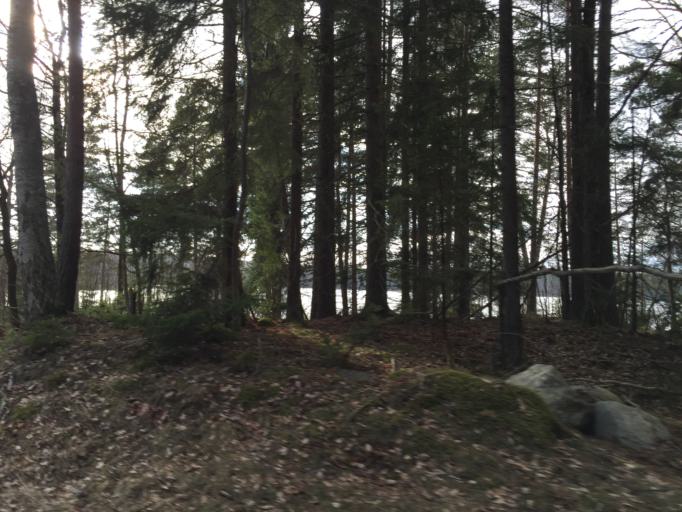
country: SE
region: Soedermanland
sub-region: Vingakers Kommun
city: Vingaker
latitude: 59.0020
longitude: 15.6758
